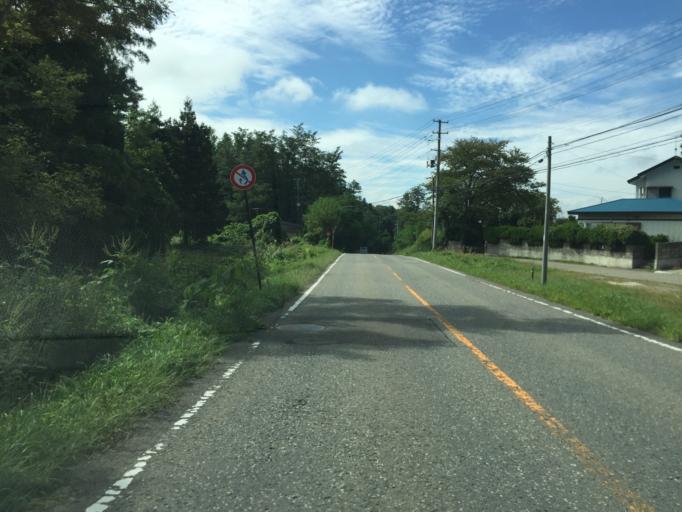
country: JP
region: Fukushima
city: Inawashiro
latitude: 37.5555
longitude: 139.9823
